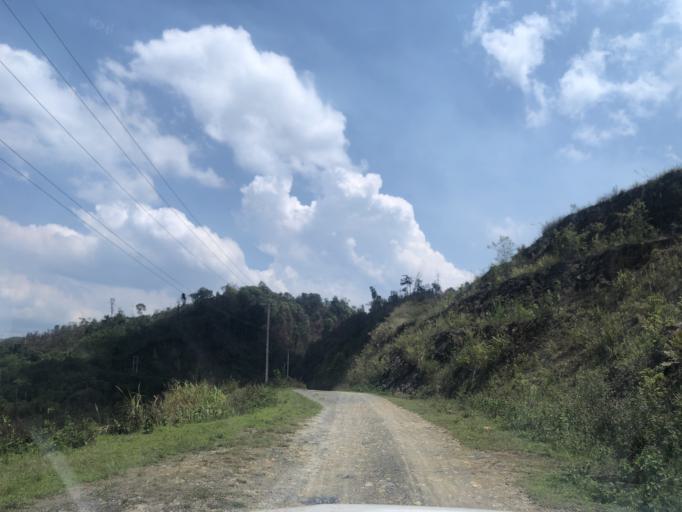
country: LA
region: Phongsali
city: Phongsali
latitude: 21.4009
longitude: 102.1890
